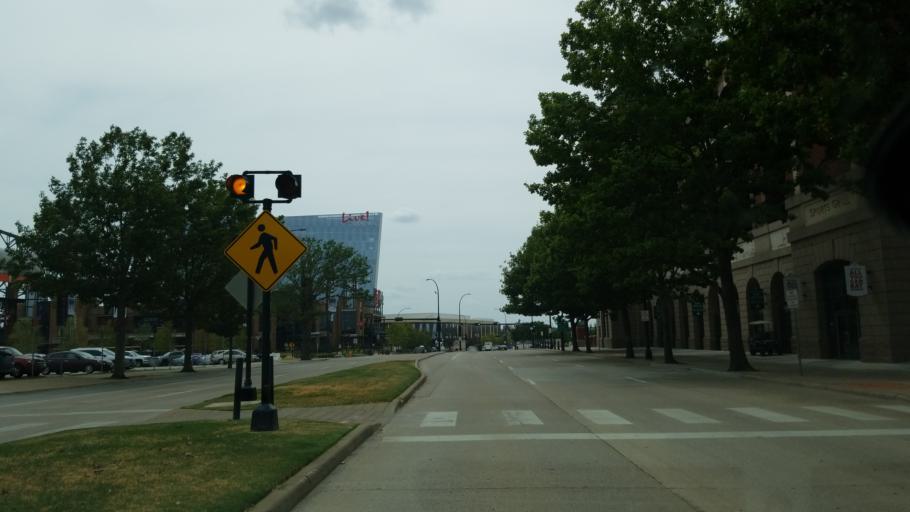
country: US
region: Texas
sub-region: Tarrant County
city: Arlington
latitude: 32.7501
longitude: -97.0827
